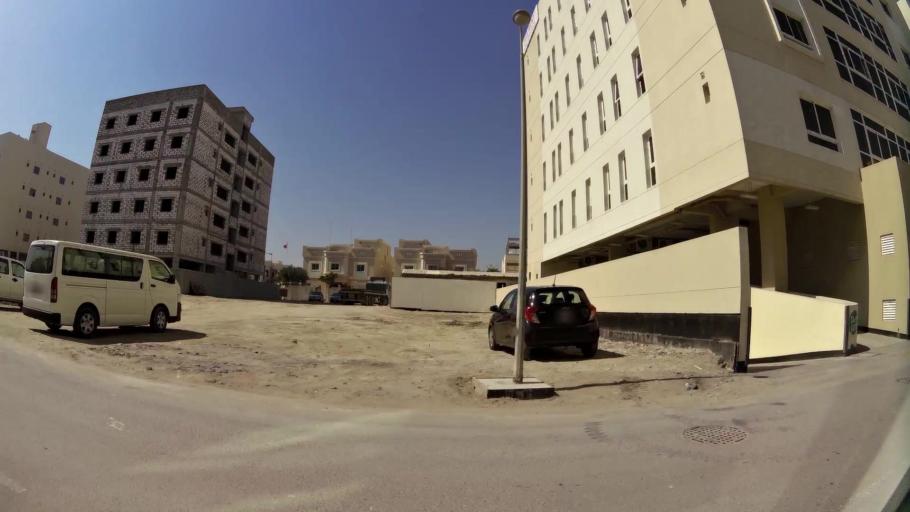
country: BH
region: Manama
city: Manama
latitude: 26.2105
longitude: 50.5991
